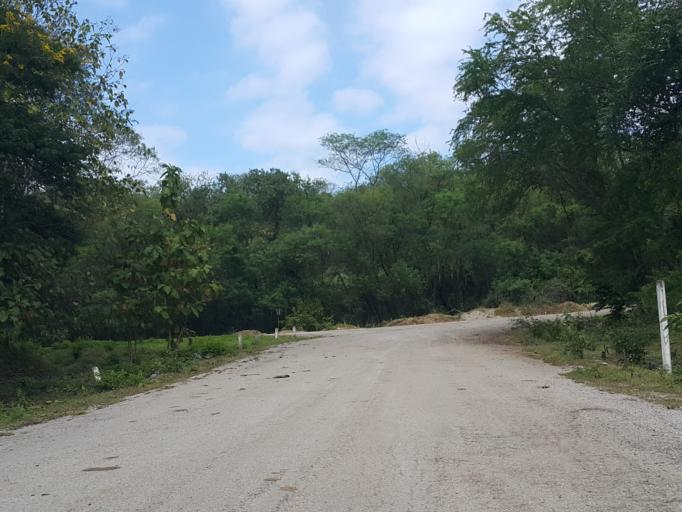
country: TH
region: Lampang
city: Mae Mo
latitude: 18.3264
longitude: 99.7519
